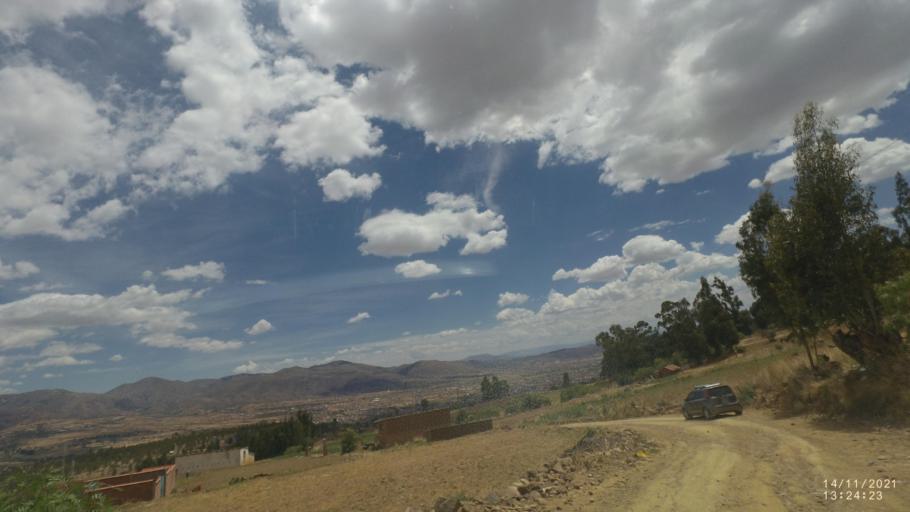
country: BO
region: Cochabamba
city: Colomi
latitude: -17.3776
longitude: -65.9802
